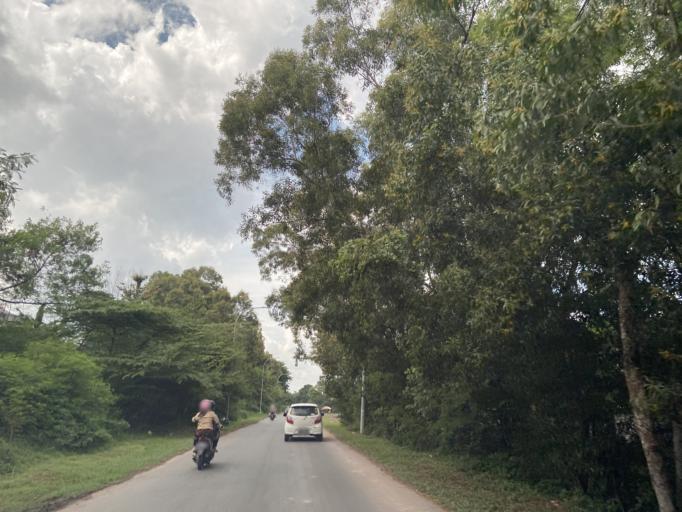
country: SG
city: Singapore
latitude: 1.1227
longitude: 104.0201
